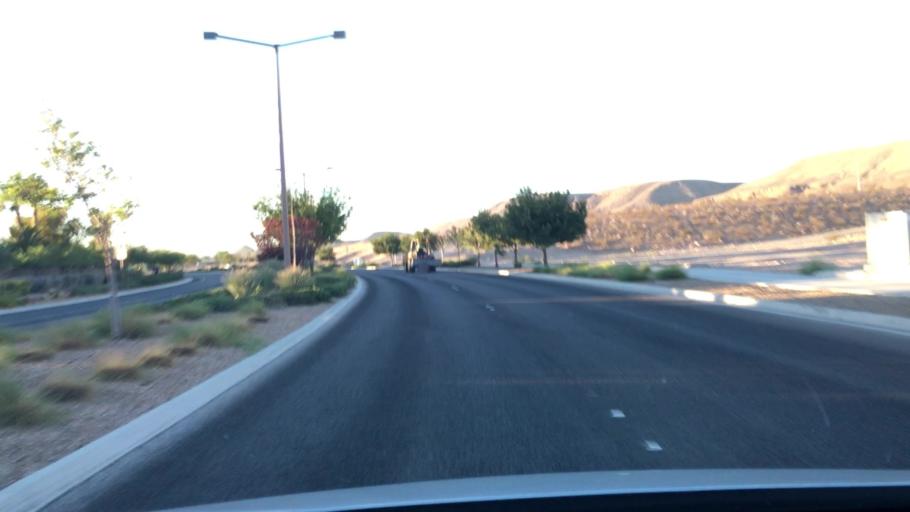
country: US
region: Nevada
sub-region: Clark County
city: Summerlin South
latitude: 36.1031
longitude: -115.3277
